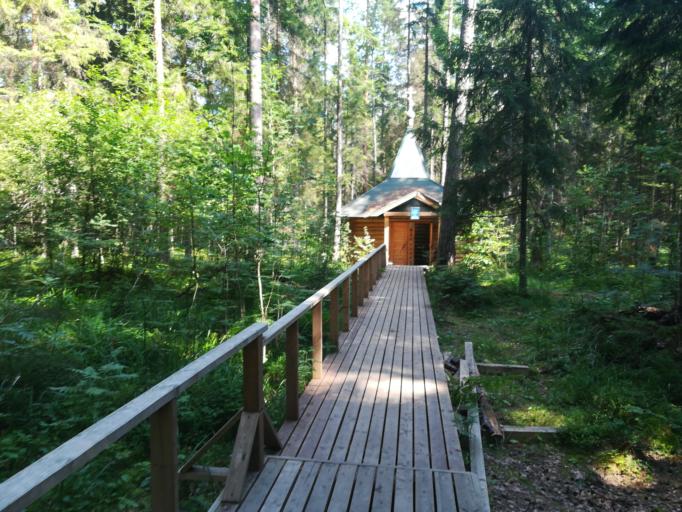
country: RU
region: Leningrad
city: Ust'-Luga
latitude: 59.7034
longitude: 28.2060
